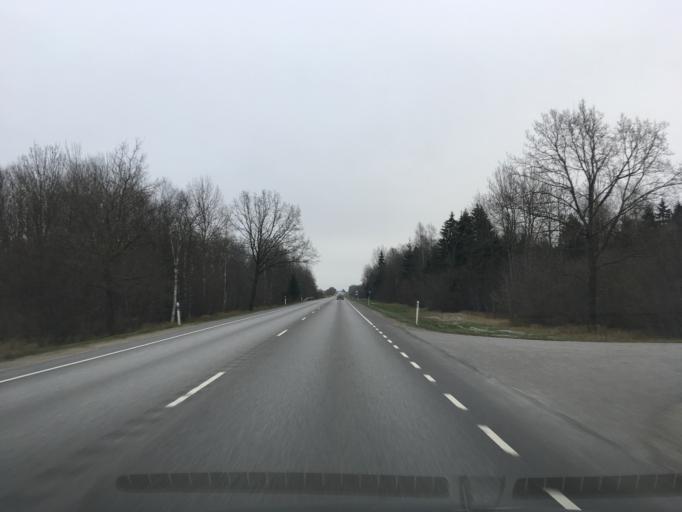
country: EE
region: Ida-Virumaa
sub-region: Kohtla-Jaerve linn
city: Kohtla-Jarve
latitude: 59.4165
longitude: 27.2923
